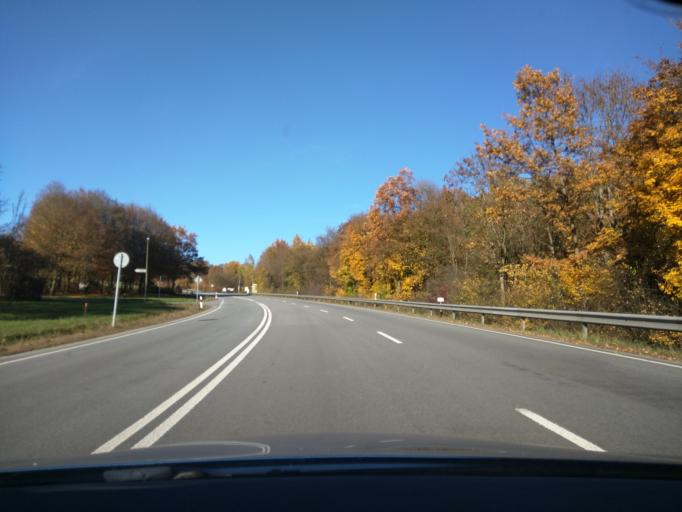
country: DE
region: Bavaria
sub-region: Lower Bavaria
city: Salzweg
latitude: 48.5907
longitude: 13.4779
